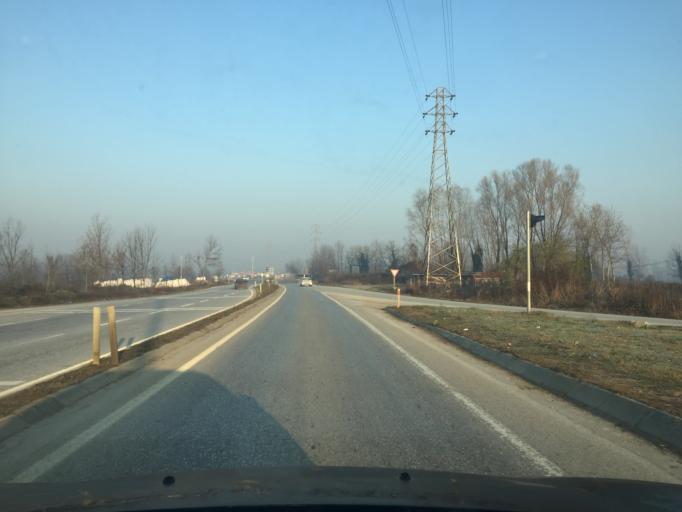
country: TR
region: Sakarya
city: Akyazi
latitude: 40.6745
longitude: 30.5856
